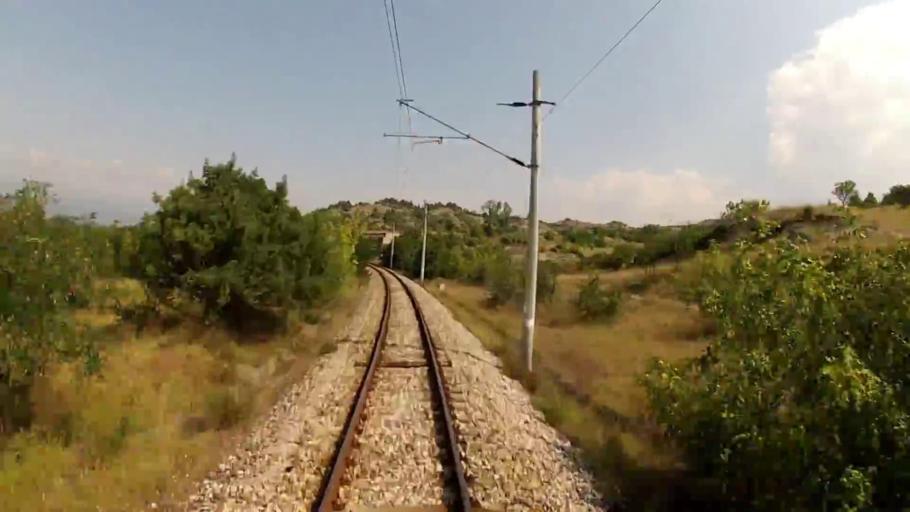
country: BG
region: Blagoevgrad
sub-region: Obshtina Strumyani
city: Strumyani
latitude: 41.6034
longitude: 23.2267
